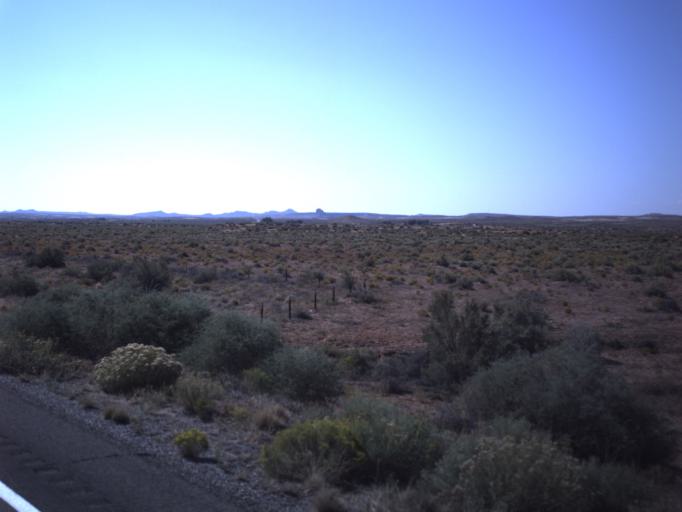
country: US
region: Utah
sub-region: San Juan County
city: Blanding
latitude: 37.1260
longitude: -109.5472
